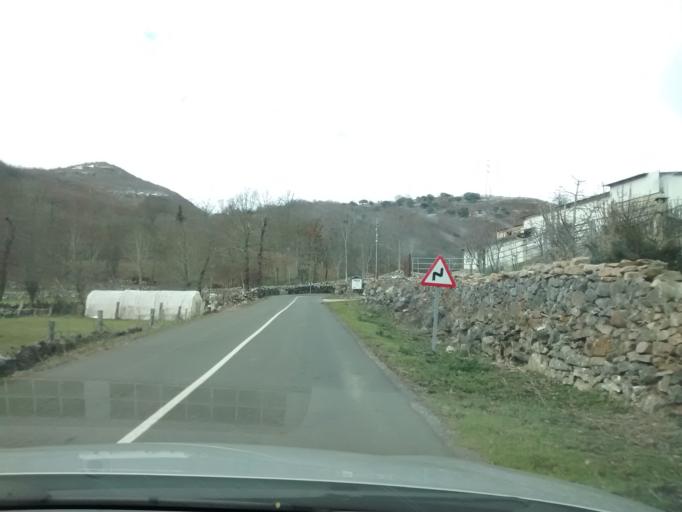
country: ES
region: Castille and Leon
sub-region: Provincia de Burgos
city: Espinosa de los Monteros
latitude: 43.1180
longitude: -3.5973
